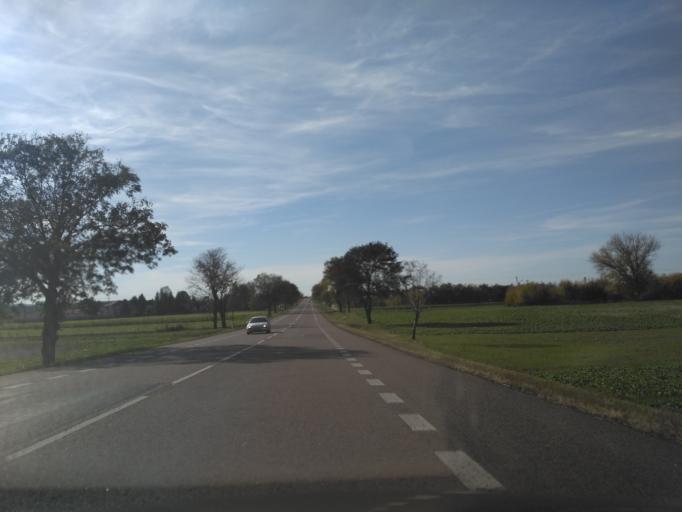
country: PL
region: Lublin Voivodeship
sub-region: Powiat swidnicki
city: Trawniki
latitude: 51.1687
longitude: 23.0913
